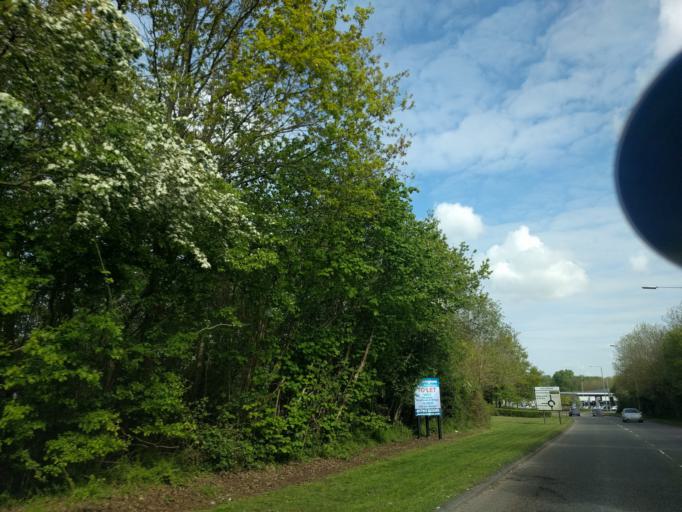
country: GB
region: England
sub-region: Wiltshire
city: Lydiard Tregoze
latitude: 51.5714
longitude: -1.8291
